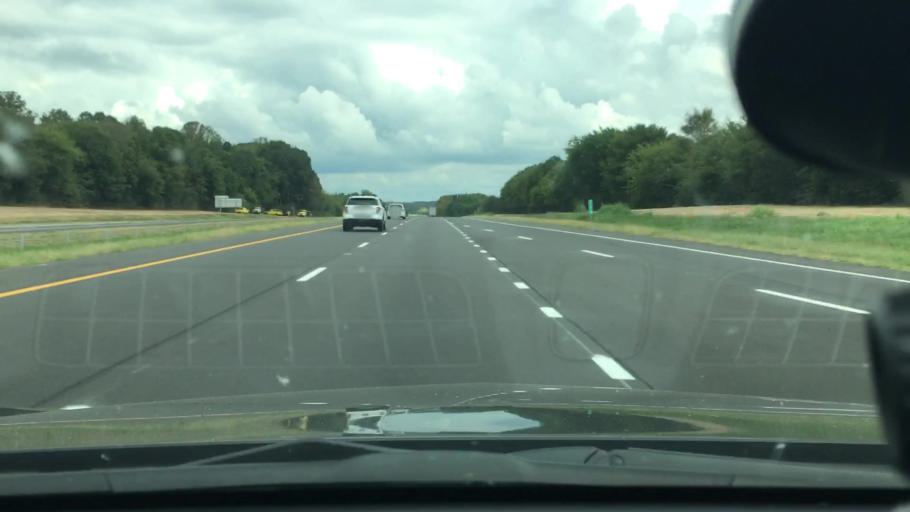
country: US
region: North Carolina
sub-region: Davie County
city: Mocksville
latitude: 35.9586
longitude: -80.5292
